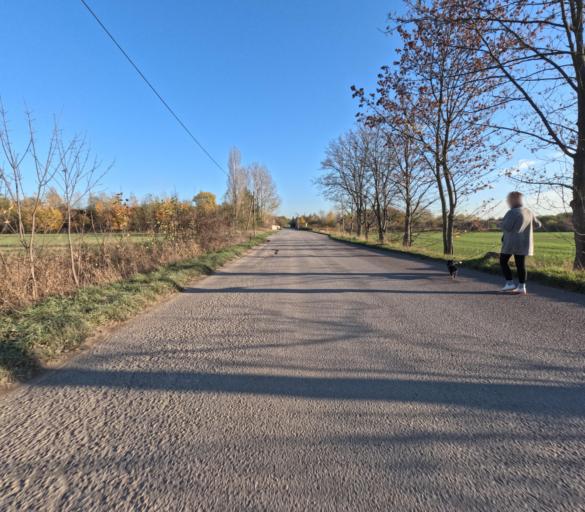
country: DE
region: Saxony
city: Otterwisch
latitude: 51.2510
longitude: 12.6479
